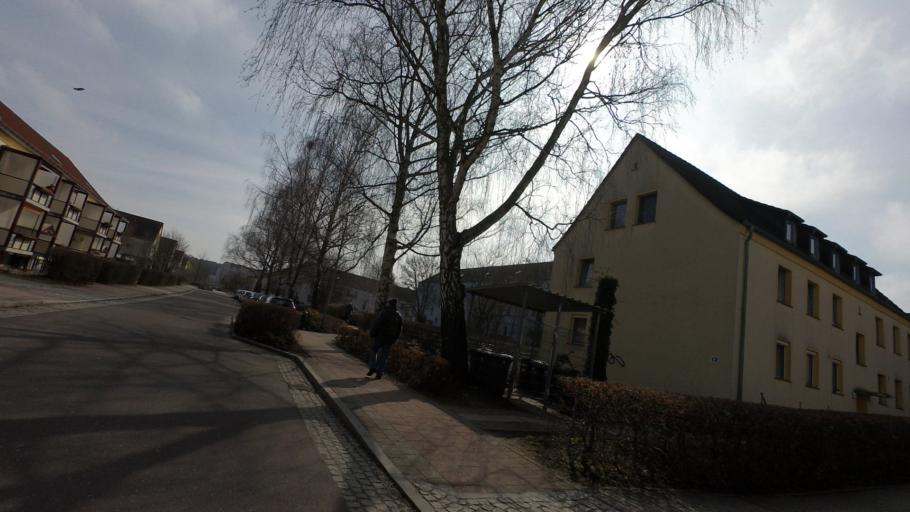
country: DE
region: Brandenburg
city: Belzig
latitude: 52.1416
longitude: 12.6023
